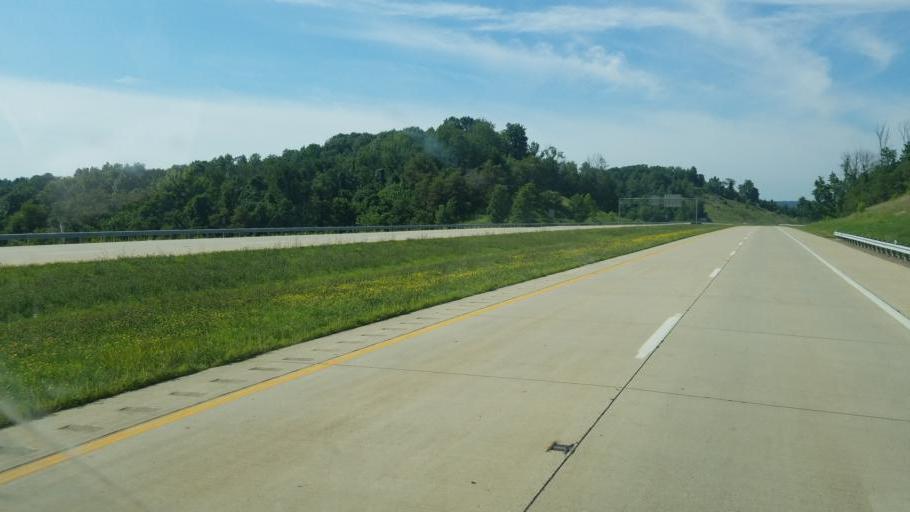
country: US
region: Ohio
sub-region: Athens County
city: Athens
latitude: 39.2889
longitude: -82.1021
